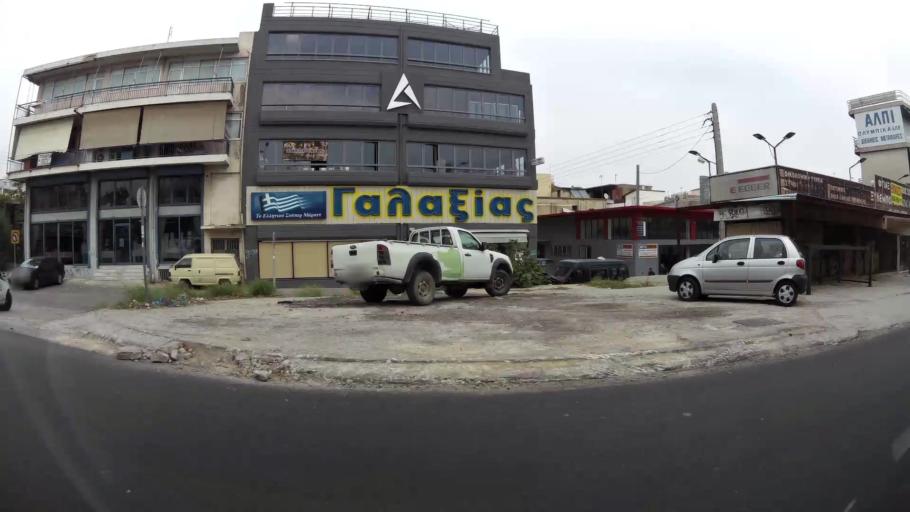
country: GR
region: Attica
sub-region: Nomarchia Athinas
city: Chaidari
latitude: 38.0071
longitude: 23.6739
